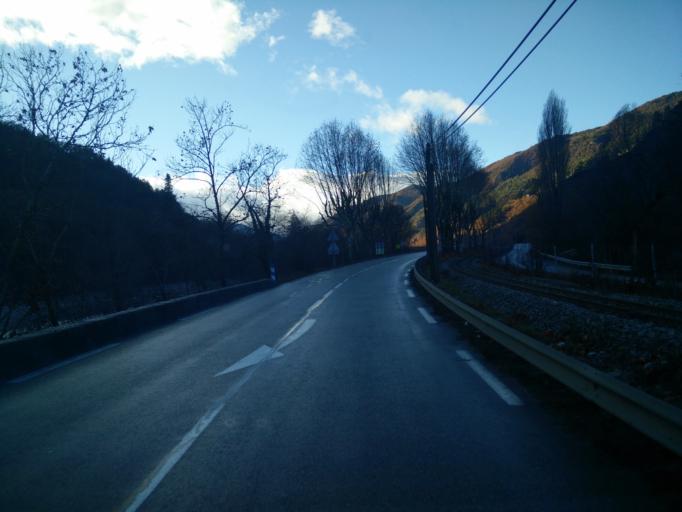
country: FR
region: Provence-Alpes-Cote d'Azur
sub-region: Departement des Alpes-Maritimes
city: Puget-Theniers
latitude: 43.9520
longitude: 6.8802
